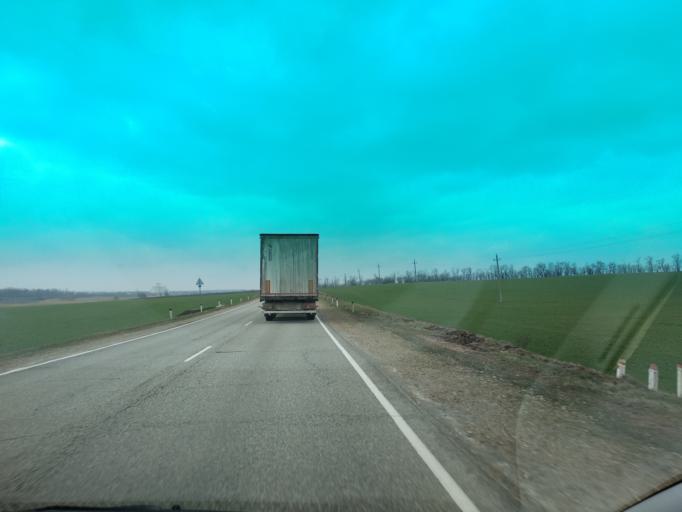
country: RU
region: Krasnodarskiy
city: Novomalorossiyskaya
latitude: 45.7193
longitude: 39.8852
